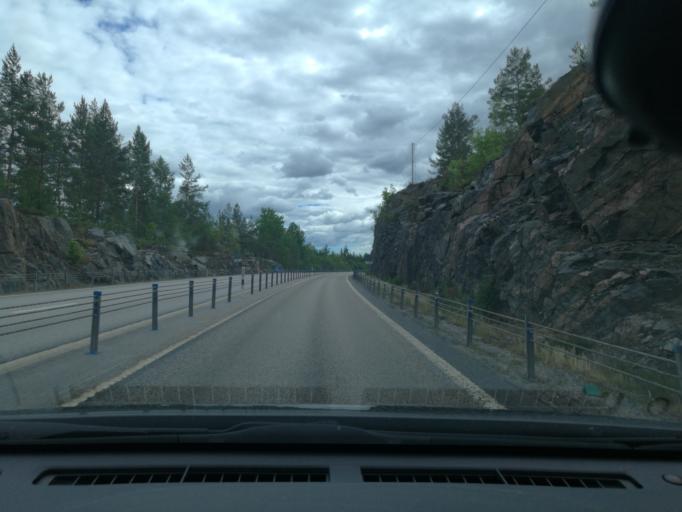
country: SE
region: OEstergoetland
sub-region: Valdemarsviks Kommun
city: Valdemarsvik
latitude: 58.1552
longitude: 16.5437
